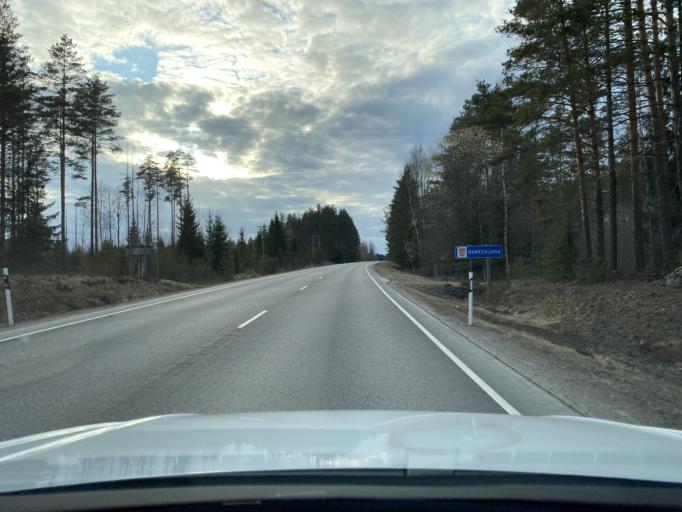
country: FI
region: Haeme
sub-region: Haemeenlinna
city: Renko
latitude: 60.7957
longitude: 24.0996
